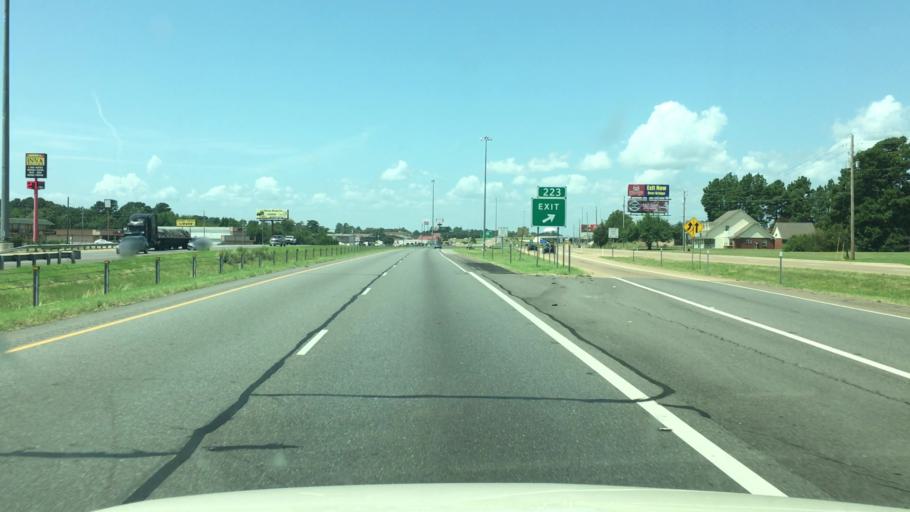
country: US
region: Arkansas
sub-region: Miller County
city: Texarkana
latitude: 33.4711
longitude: -94.0308
